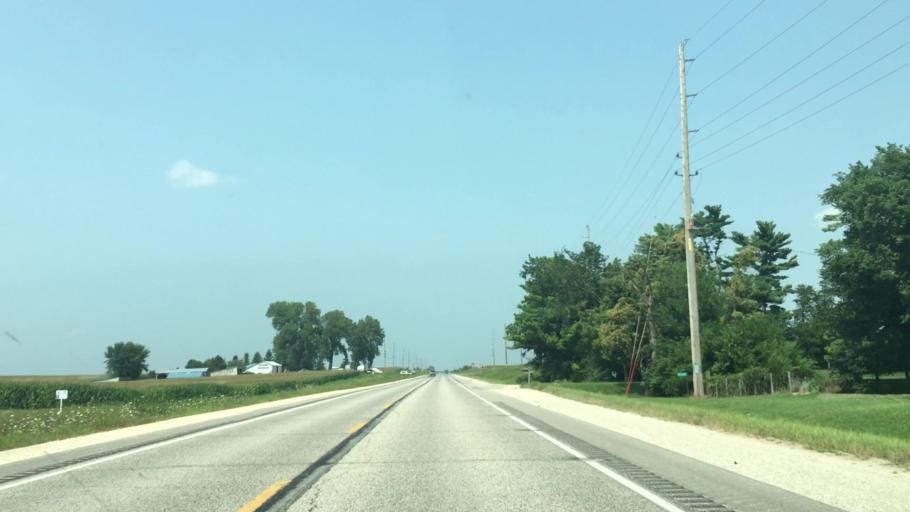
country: US
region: Iowa
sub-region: Fayette County
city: Fayette
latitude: 42.8799
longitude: -91.8105
